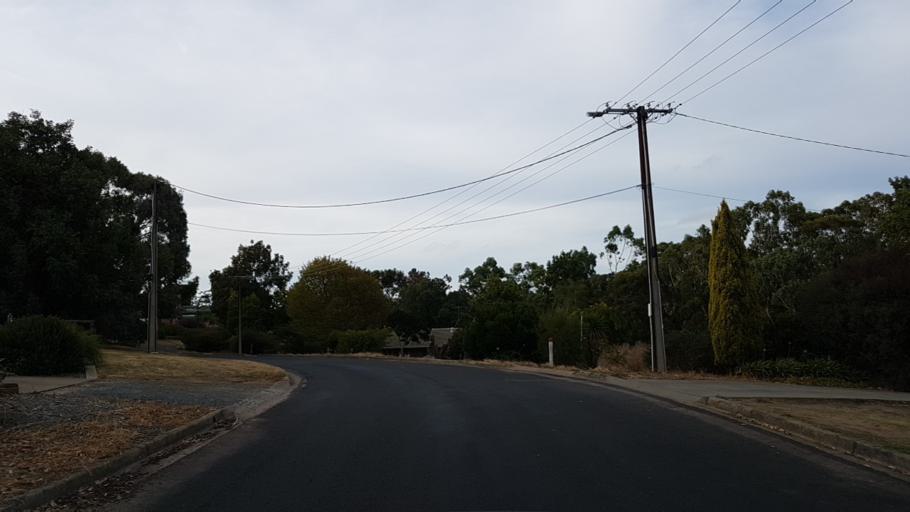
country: AU
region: South Australia
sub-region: Mount Barker
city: Nairne
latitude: -35.0313
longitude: 138.9102
